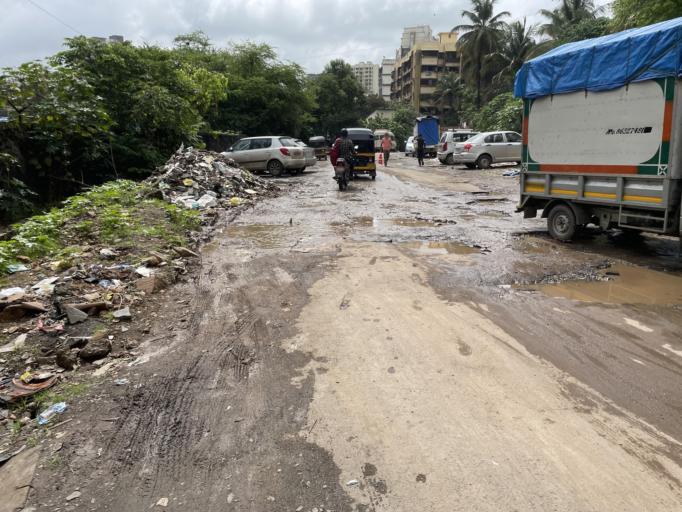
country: IN
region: Maharashtra
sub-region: Mumbai Suburban
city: Borivli
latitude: 19.2386
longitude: 72.8653
